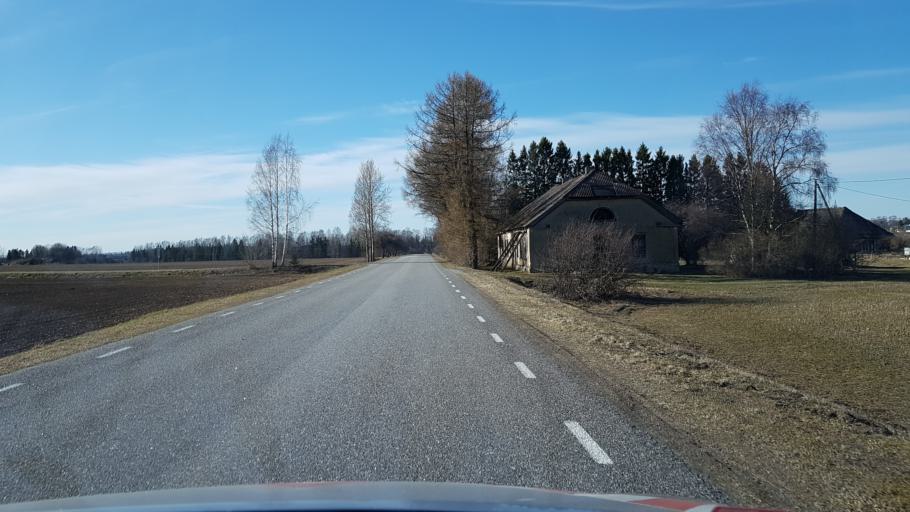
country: EE
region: Laeaene-Virumaa
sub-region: Kadrina vald
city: Kadrina
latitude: 59.3326
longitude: 26.1309
